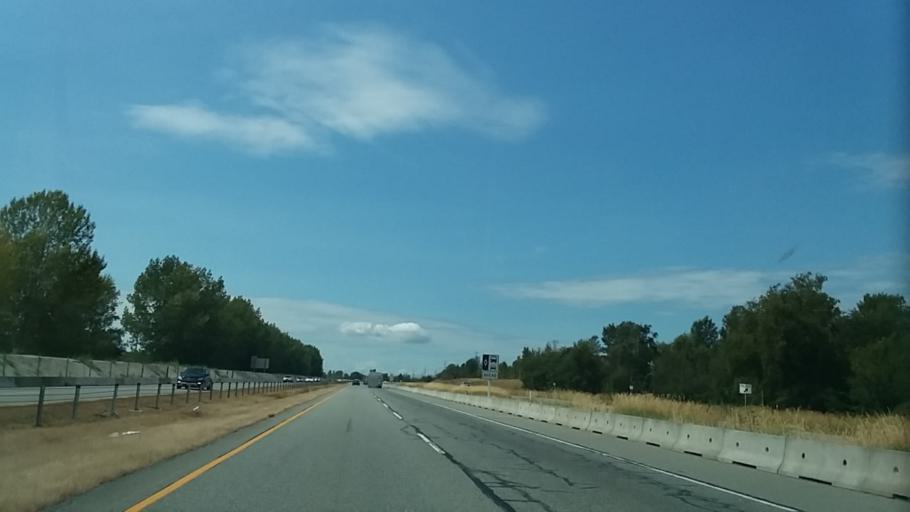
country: CA
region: British Columbia
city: Ladner
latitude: 49.0908
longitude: -122.9914
